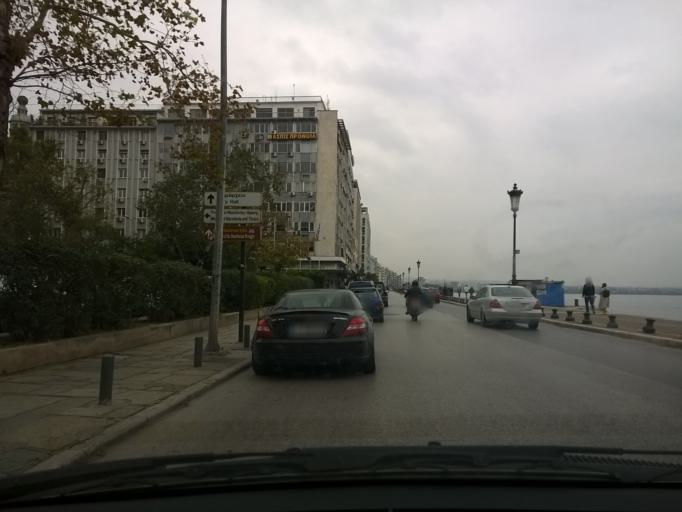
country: GR
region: Central Macedonia
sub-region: Nomos Thessalonikis
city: Thessaloniki
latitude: 40.6337
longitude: 22.9375
